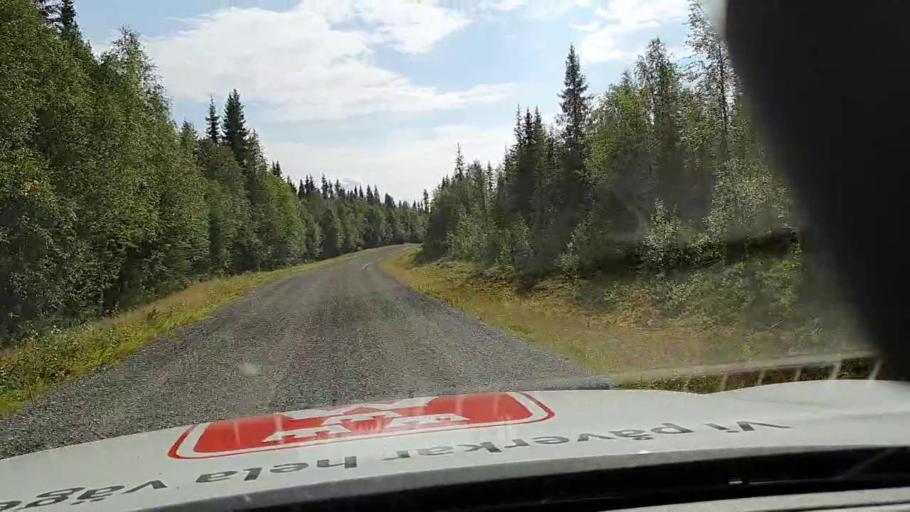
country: SE
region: Vaesterbotten
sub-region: Storumans Kommun
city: Fristad
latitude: 65.5438
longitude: 16.7951
